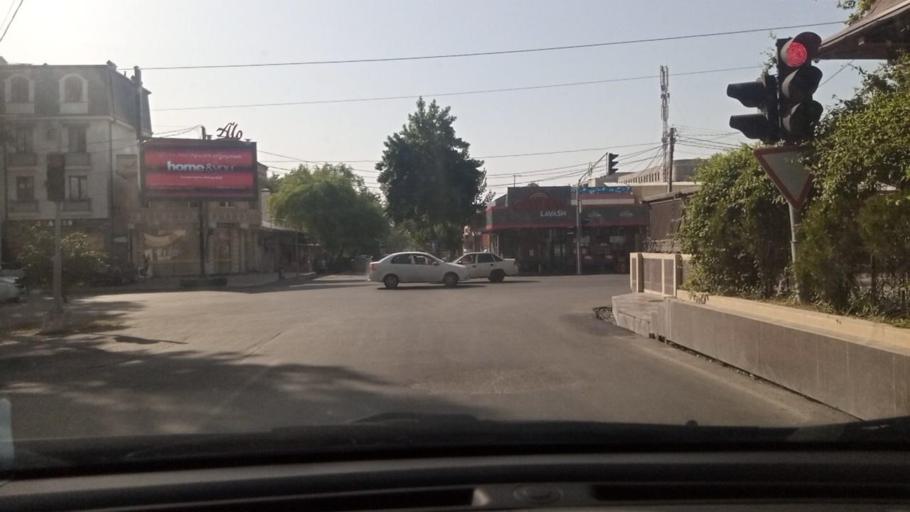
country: UZ
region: Toshkent
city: Salor
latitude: 41.3377
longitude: 69.3554
